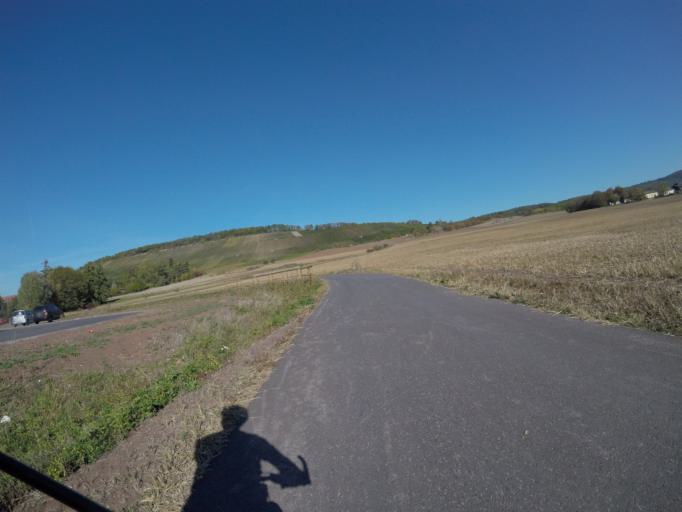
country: DE
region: Baden-Wuerttemberg
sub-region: Karlsruhe Region
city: Illingen
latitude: 48.9934
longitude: 8.9499
